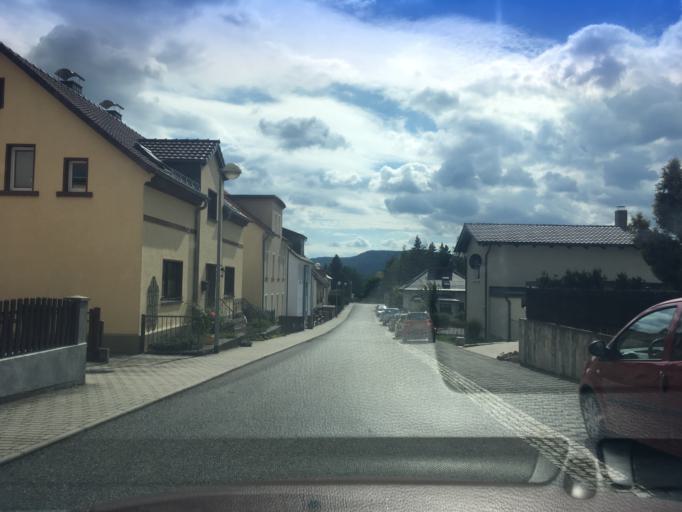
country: DE
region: Saxony
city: Mittelherwigsdorf
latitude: 50.9011
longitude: 14.7751
